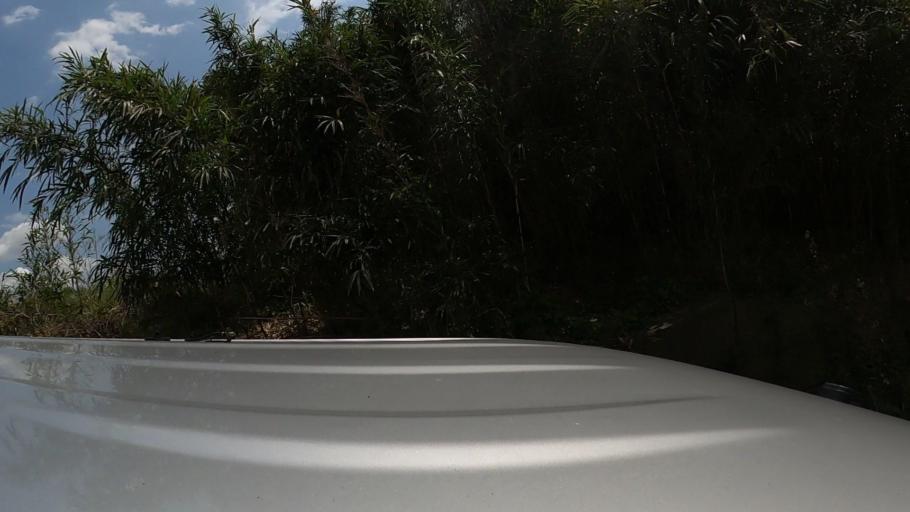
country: JP
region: Kanagawa
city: Chigasaki
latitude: 35.3884
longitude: 139.4199
